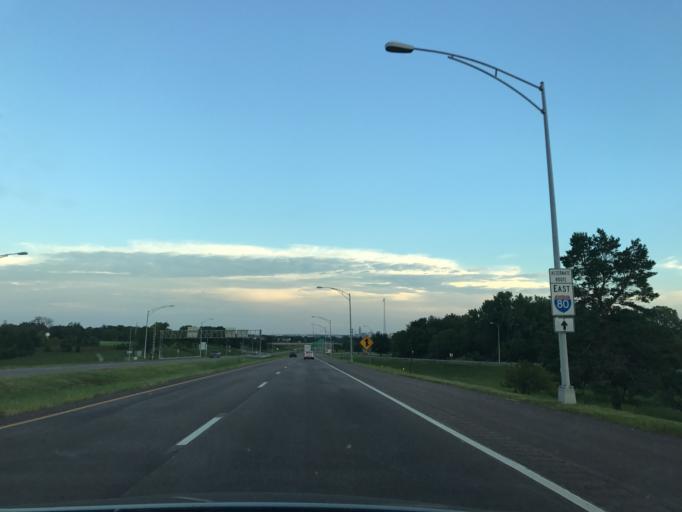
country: US
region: Nebraska
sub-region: Lancaster County
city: Lincoln
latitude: 40.8609
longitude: -96.7155
